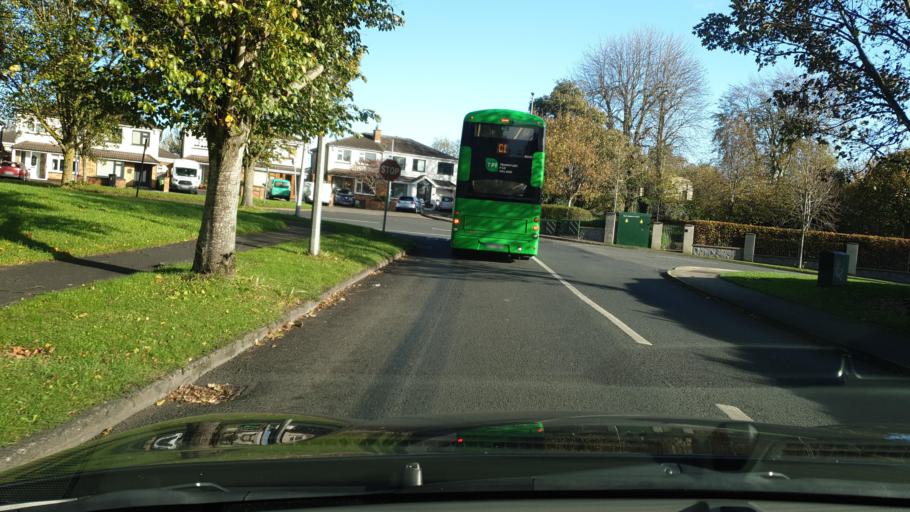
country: IE
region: Leinster
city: Lucan
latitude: 53.3493
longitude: -6.4391
